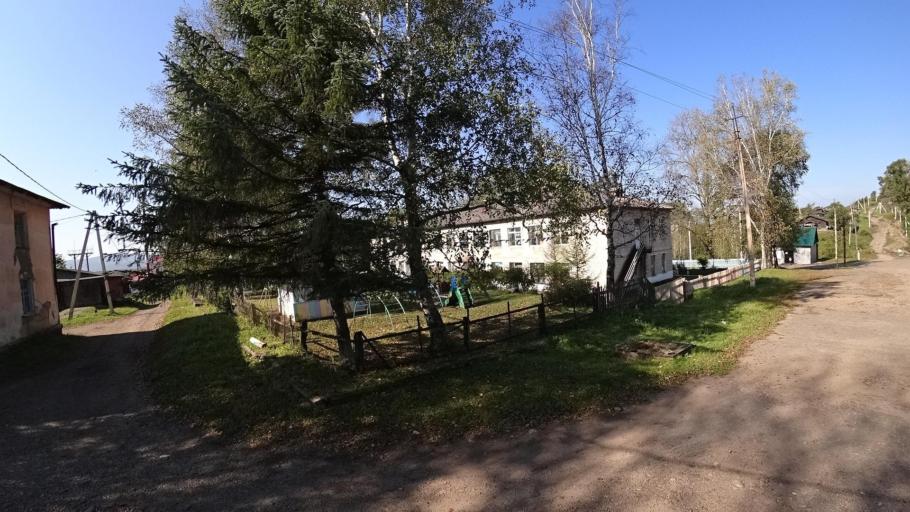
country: RU
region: Jewish Autonomous Oblast
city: Bira
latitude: 49.0015
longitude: 132.4652
